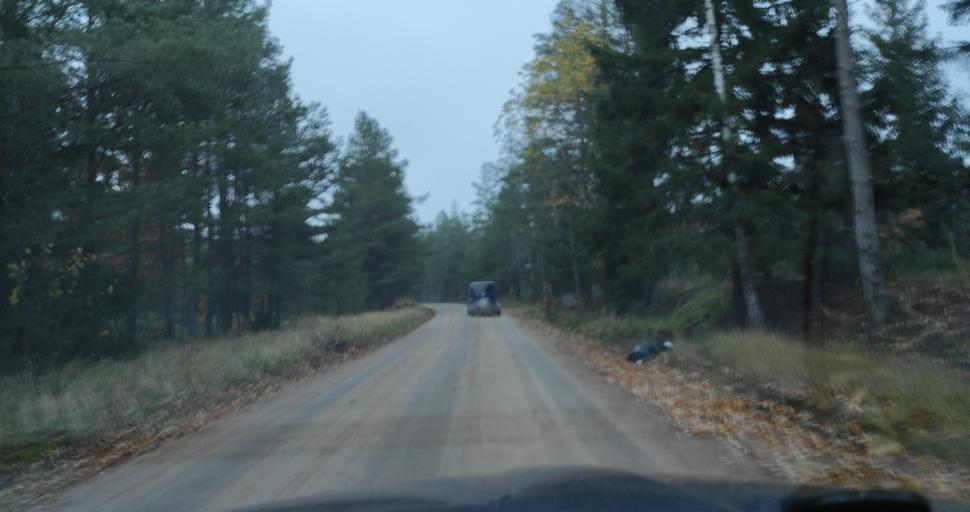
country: LV
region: Pavilostas
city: Pavilosta
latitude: 56.7587
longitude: 21.2711
